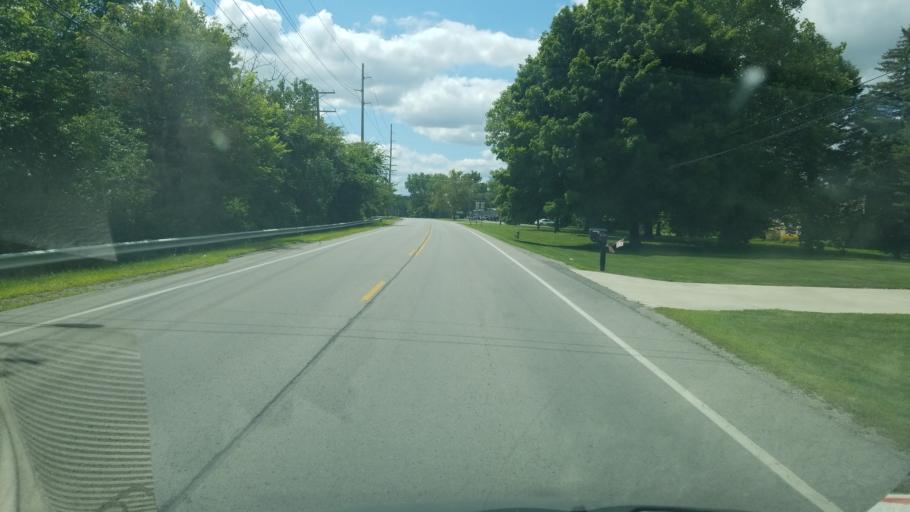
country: US
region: Ohio
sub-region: Henry County
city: Napoleon
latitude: 41.4069
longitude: -84.1035
